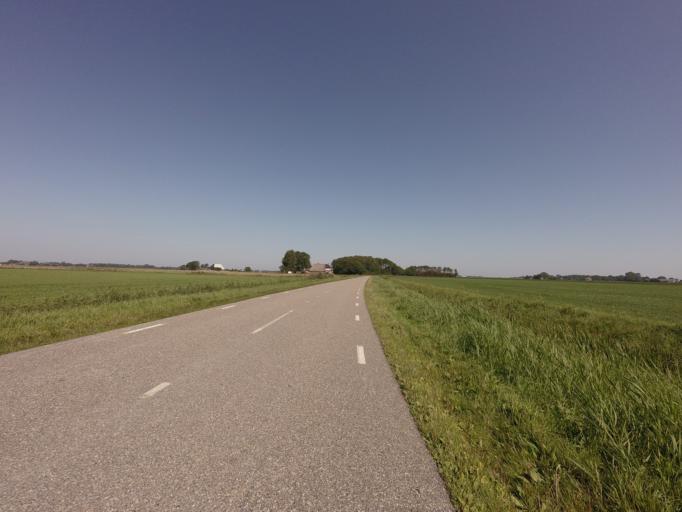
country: NL
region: Friesland
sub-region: Gemeente Dongeradeel
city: Ternaard
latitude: 53.3644
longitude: 5.9811
